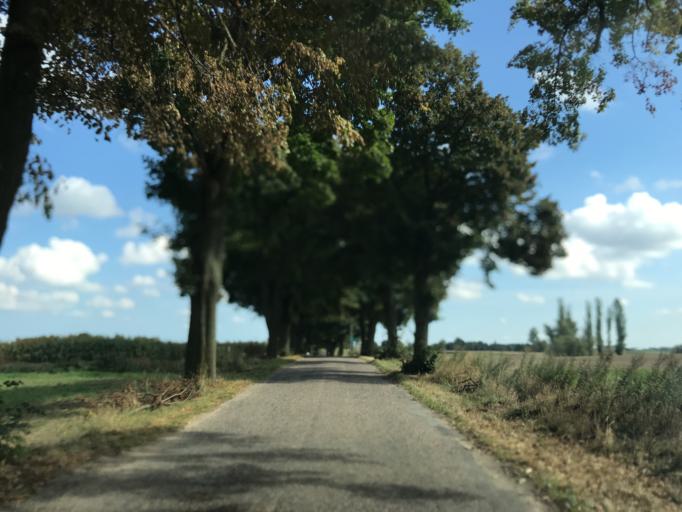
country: PL
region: Kujawsko-Pomorskie
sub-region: Powiat brodnicki
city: Brzozie
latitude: 53.3526
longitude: 19.6673
